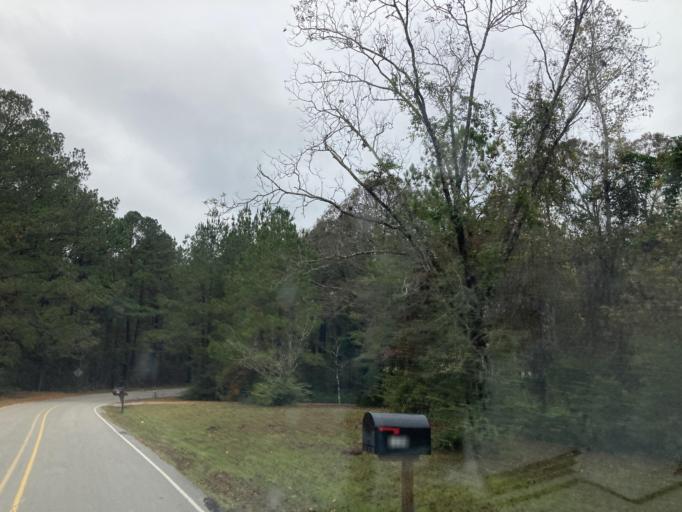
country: US
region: Mississippi
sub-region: Lamar County
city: Purvis
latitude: 31.1838
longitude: -89.4221
